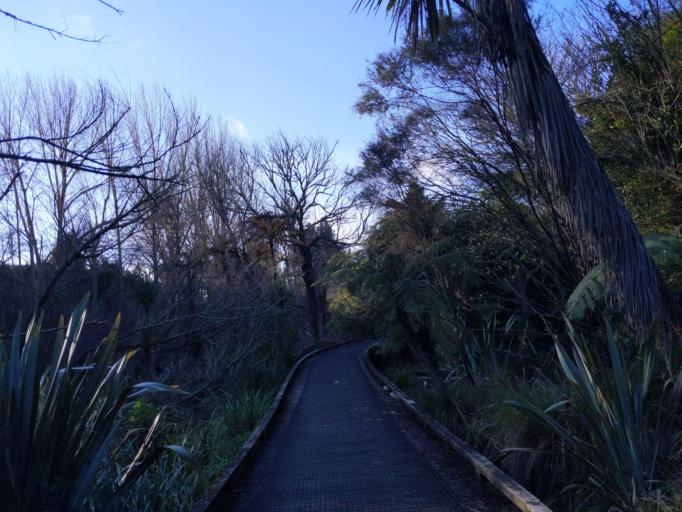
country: NZ
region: Waikato
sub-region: Hamilton City
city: Hamilton
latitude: -37.7395
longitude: 175.2759
